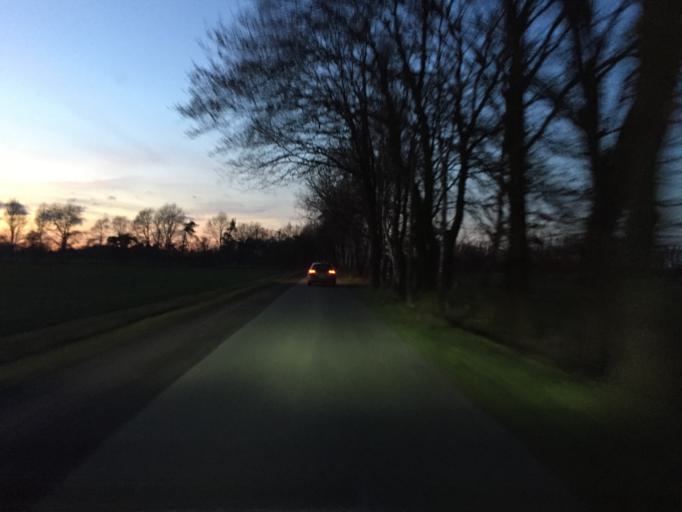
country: DE
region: Lower Saxony
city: Kirchdorf
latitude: 52.6321
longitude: 8.8601
